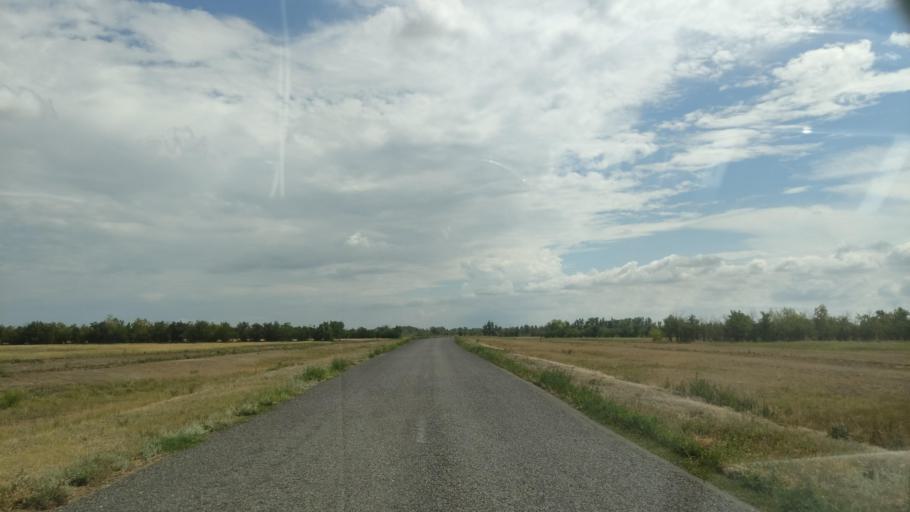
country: KZ
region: Pavlodar
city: Pavlodar
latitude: 52.6367
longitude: 76.9812
